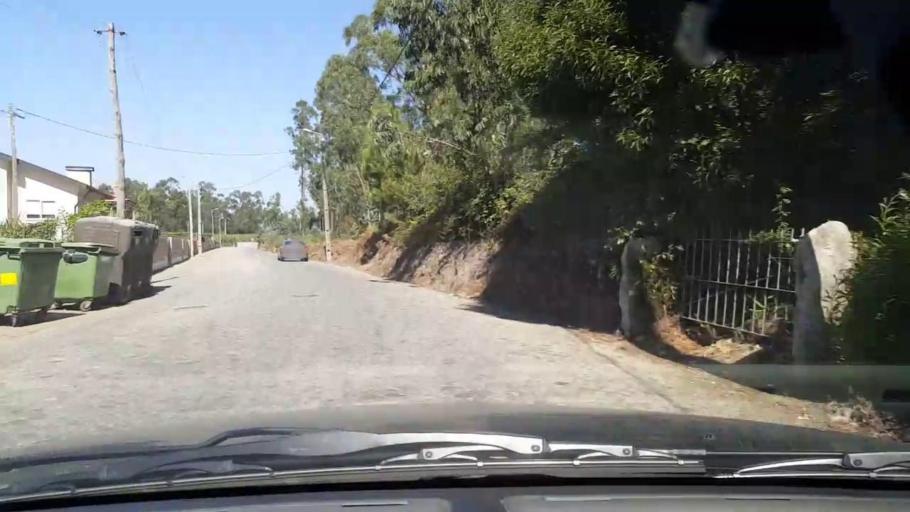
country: PT
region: Porto
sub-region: Matosinhos
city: Lavra
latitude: 41.2989
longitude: -8.7146
